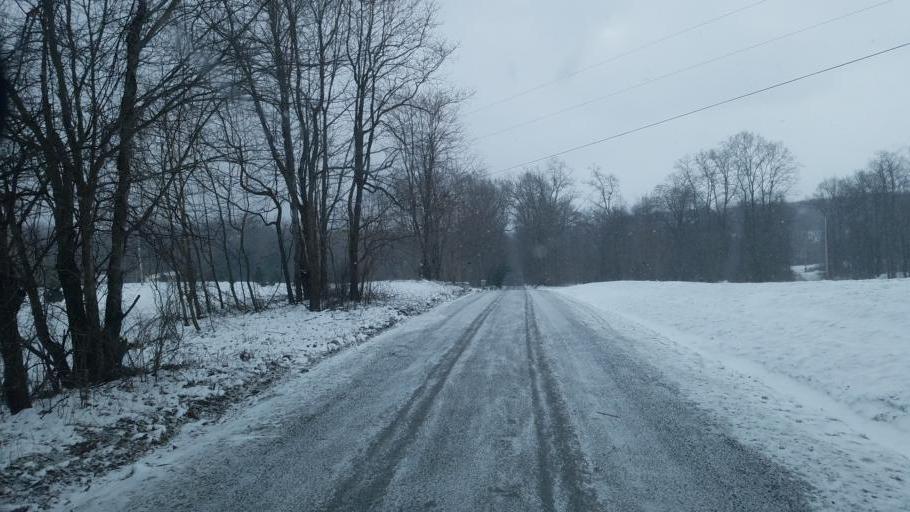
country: US
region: Pennsylvania
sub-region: Crawford County
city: Cochranton
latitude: 41.4412
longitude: -79.9843
